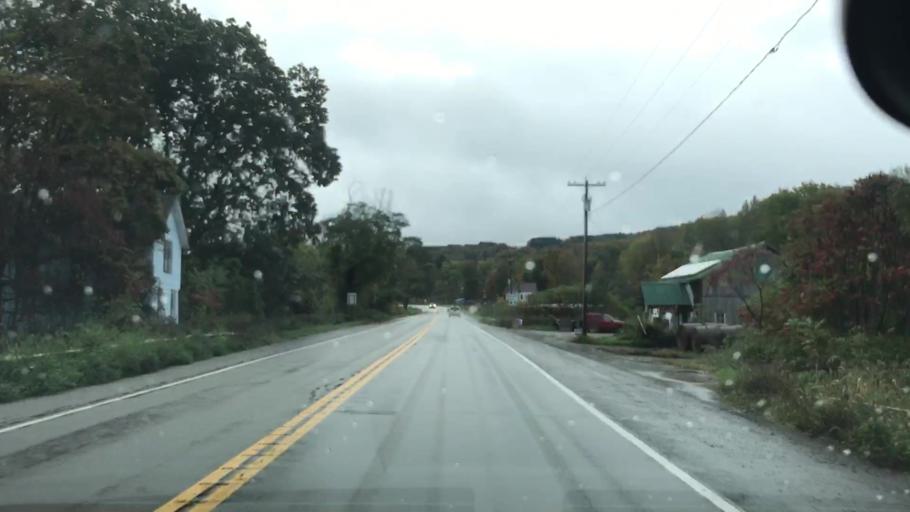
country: US
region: New York
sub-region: Erie County
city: Springville
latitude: 42.4084
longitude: -78.6890
